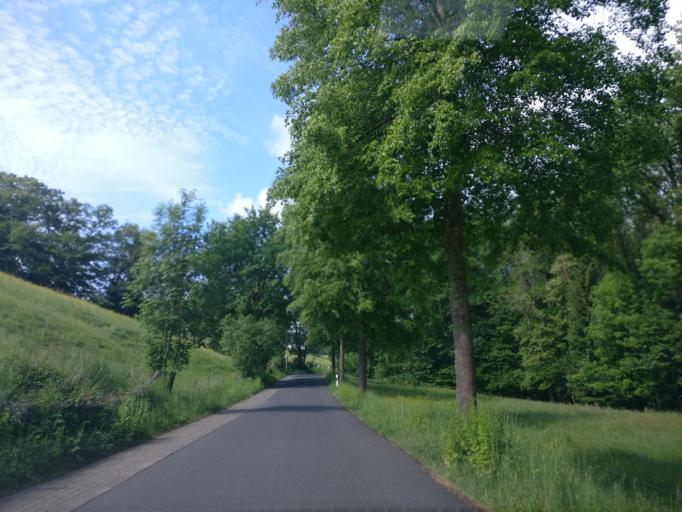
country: DE
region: Lower Saxony
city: Scheden
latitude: 51.4001
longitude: 9.7120
